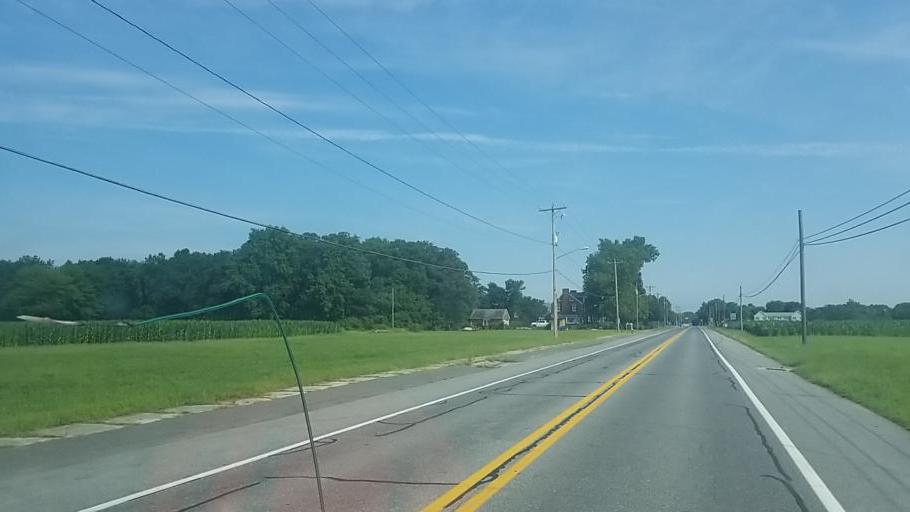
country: US
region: Delaware
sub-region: Sussex County
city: Selbyville
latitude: 38.5324
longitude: -75.2356
